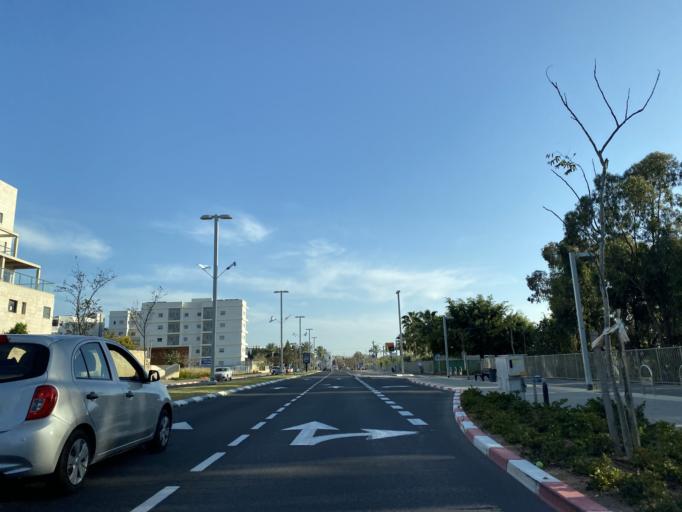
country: IL
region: Tel Aviv
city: Herzliyya
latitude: 32.1735
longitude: 34.8293
